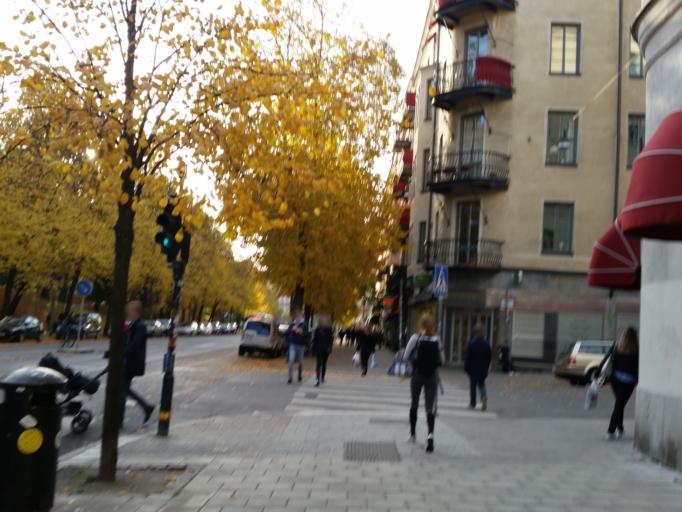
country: SE
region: Stockholm
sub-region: Stockholms Kommun
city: Stockholm
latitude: 59.3410
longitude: 18.0426
